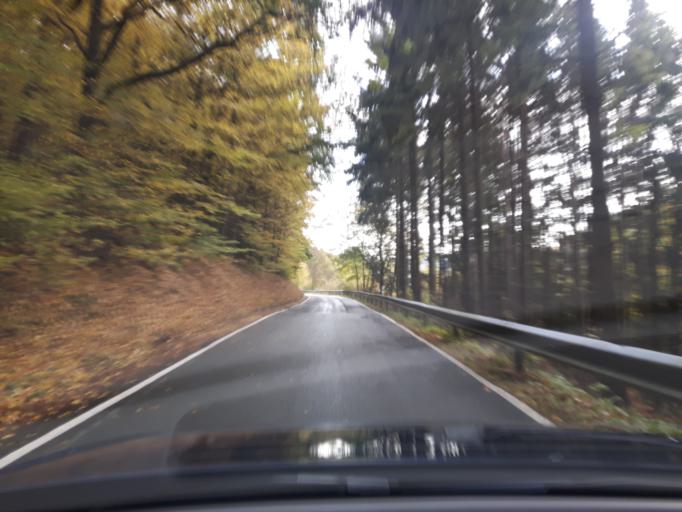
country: DE
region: North Rhine-Westphalia
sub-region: Regierungsbezirk Arnsberg
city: Bad Berleburg
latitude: 51.0175
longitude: 8.4249
